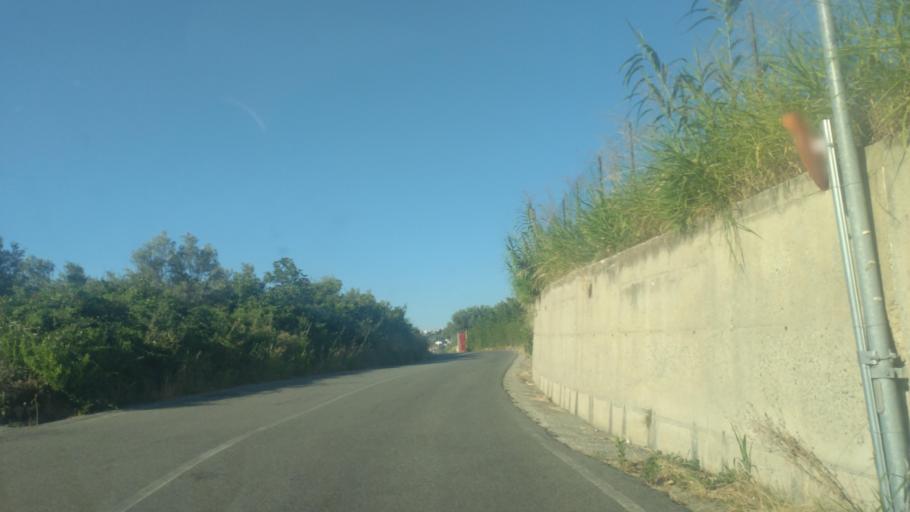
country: IT
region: Calabria
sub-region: Provincia di Catanzaro
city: Staletti
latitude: 38.7658
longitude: 16.5220
